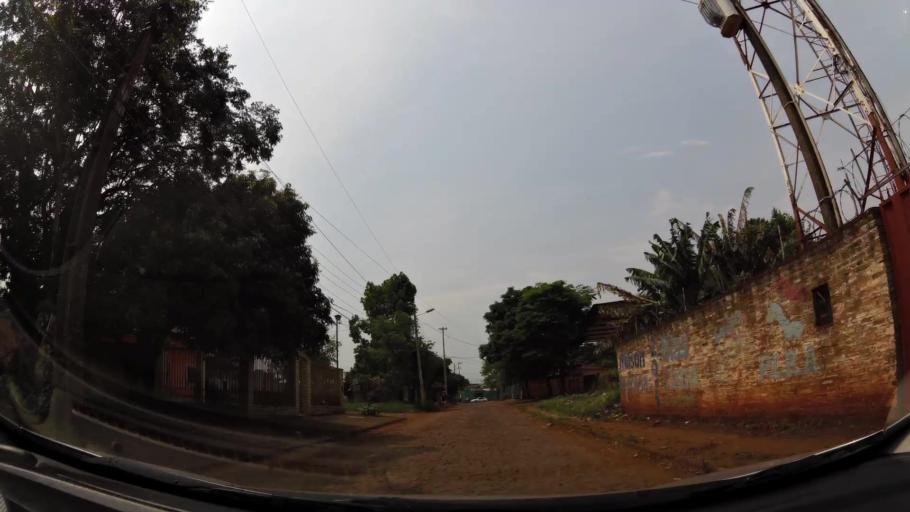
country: PY
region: Alto Parana
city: Presidente Franco
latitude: -25.5614
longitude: -54.6180
